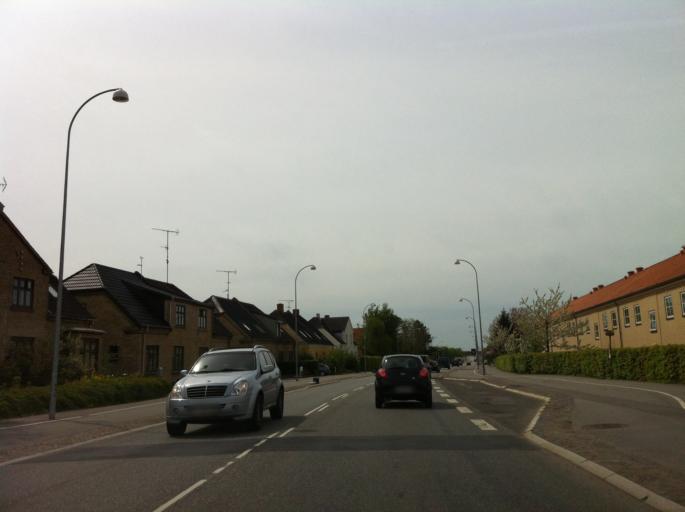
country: DK
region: Zealand
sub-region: Roskilde Kommune
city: Roskilde
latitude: 55.6317
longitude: 12.0701
